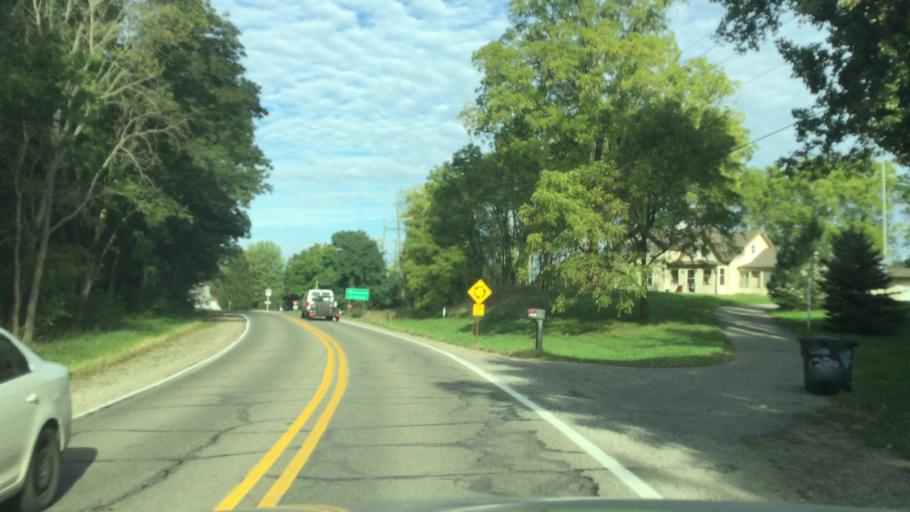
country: US
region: Michigan
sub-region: Livingston County
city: Brighton
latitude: 42.5359
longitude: -83.8690
